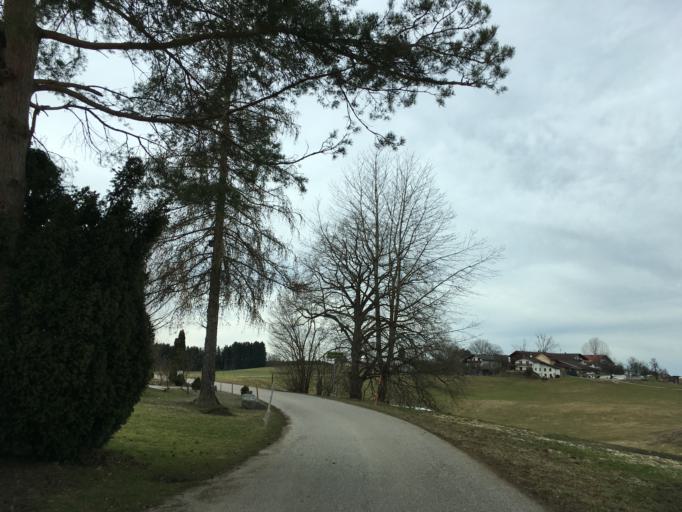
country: DE
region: Bavaria
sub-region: Upper Bavaria
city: Eggstatt
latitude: 47.9001
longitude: 12.3733
